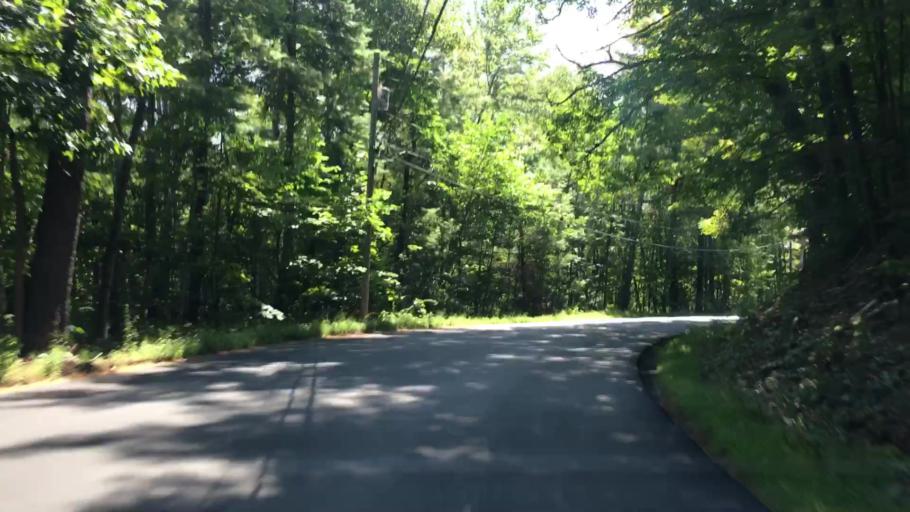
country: US
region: New Hampshire
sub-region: Rockingham County
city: Hampstead
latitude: 42.8781
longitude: -71.2182
